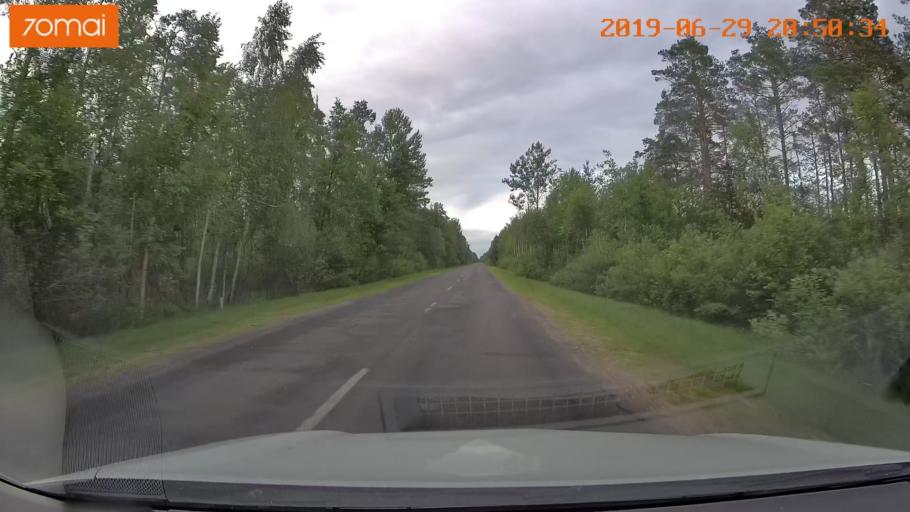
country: BY
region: Brest
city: Hantsavichy
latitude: 52.6780
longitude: 26.3377
